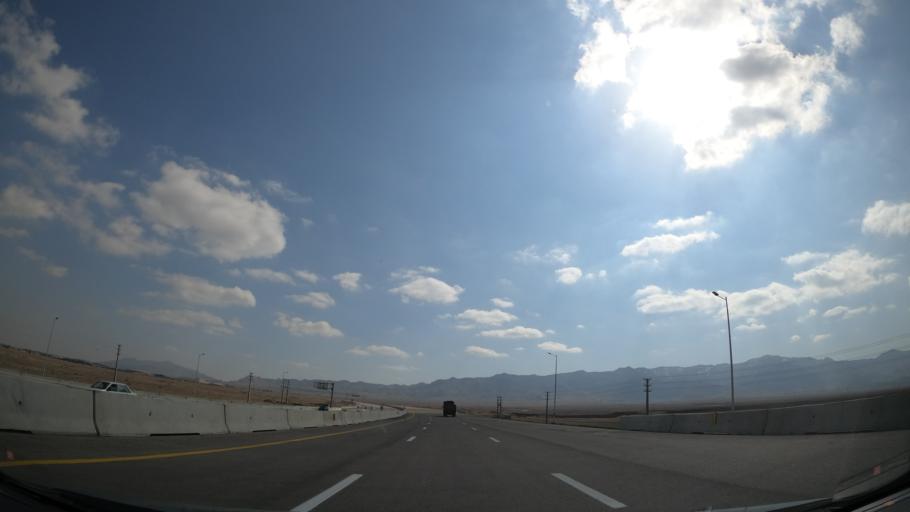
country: IR
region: Alborz
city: Eshtehard
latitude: 35.7285
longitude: 50.5620
